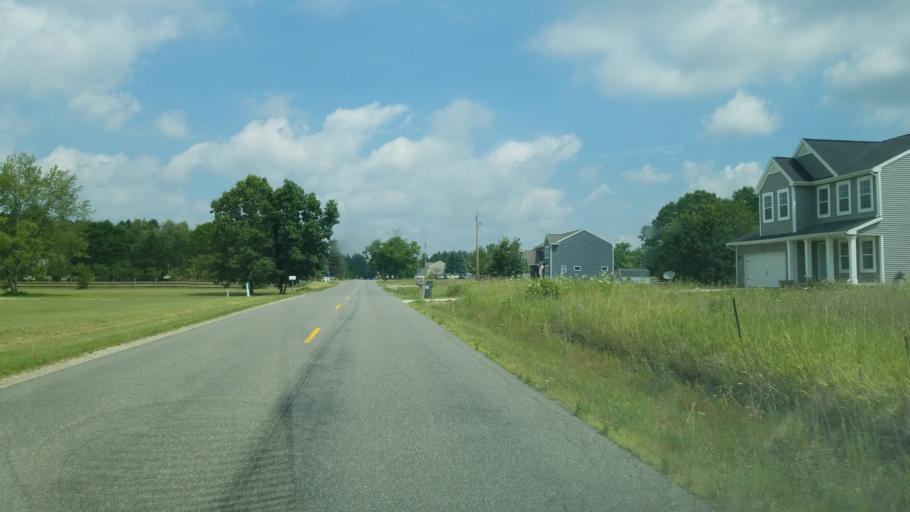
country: US
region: Michigan
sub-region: Kent County
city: Cedar Springs
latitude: 43.2311
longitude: -85.5110
